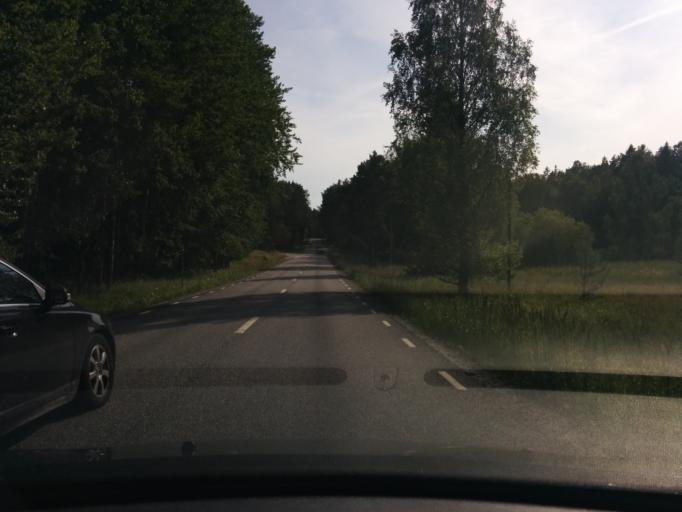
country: SE
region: Stockholm
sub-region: Varmdo Kommun
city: Holo
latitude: 59.2821
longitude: 18.6355
